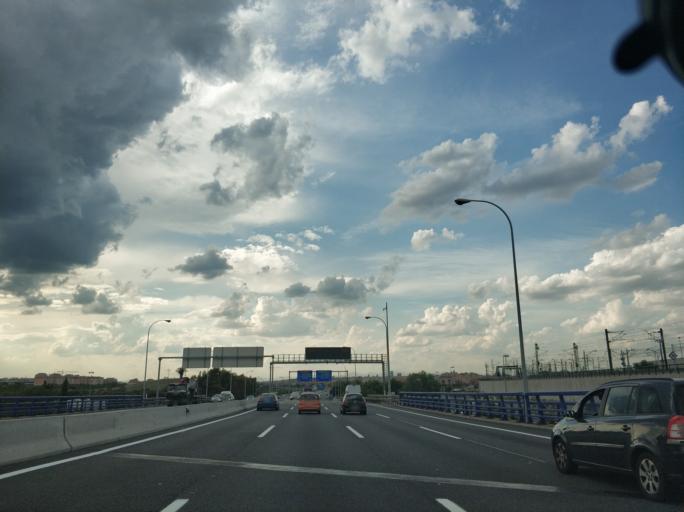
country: ES
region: Madrid
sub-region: Provincia de Madrid
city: Usera
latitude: 40.3740
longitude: -3.6816
